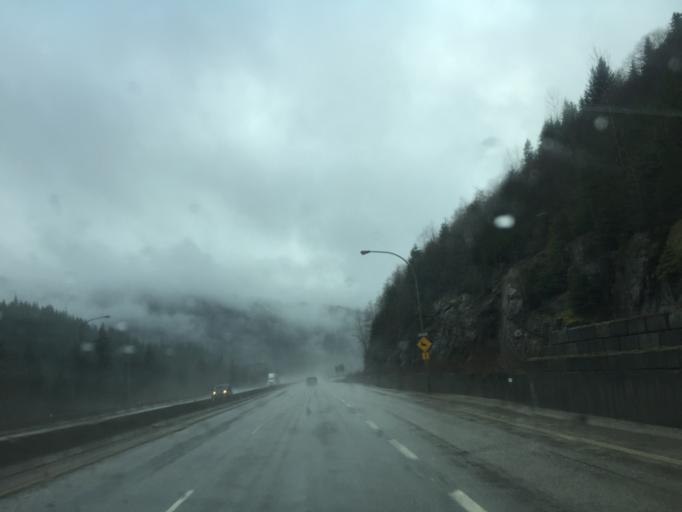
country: CA
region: British Columbia
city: Hope
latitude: 49.5033
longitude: -121.2005
